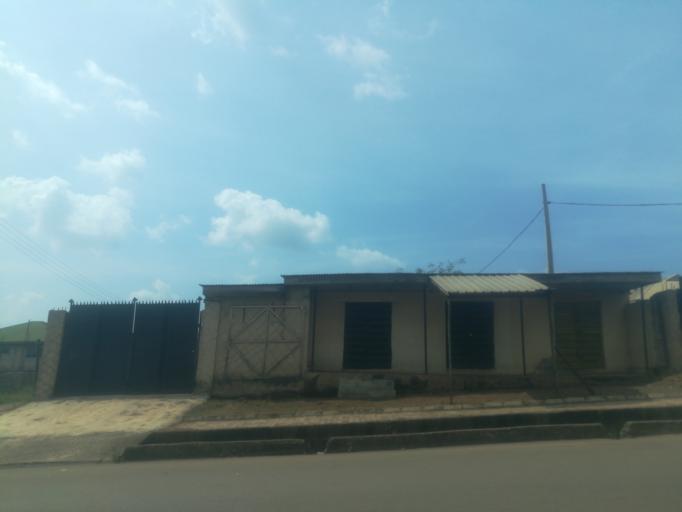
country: NG
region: Ogun
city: Abeokuta
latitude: 7.1633
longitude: 3.3764
